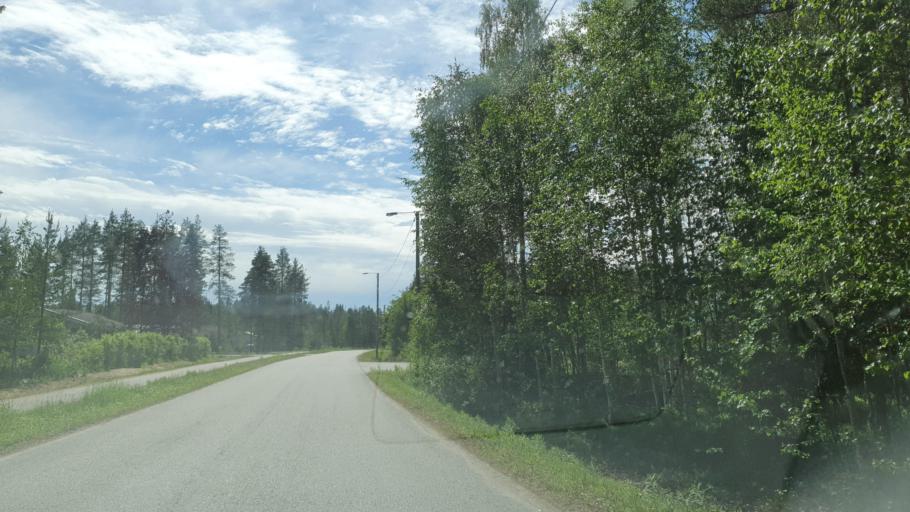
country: FI
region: Kainuu
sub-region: Kehys-Kainuu
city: Hyrynsalmi
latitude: 64.6892
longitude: 28.4693
